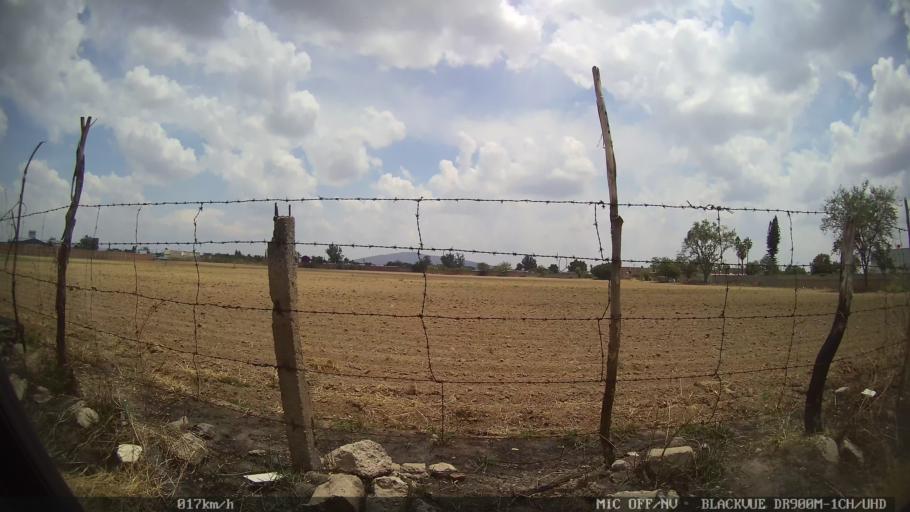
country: MX
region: Jalisco
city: Tonala
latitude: 20.6657
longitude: -103.2303
